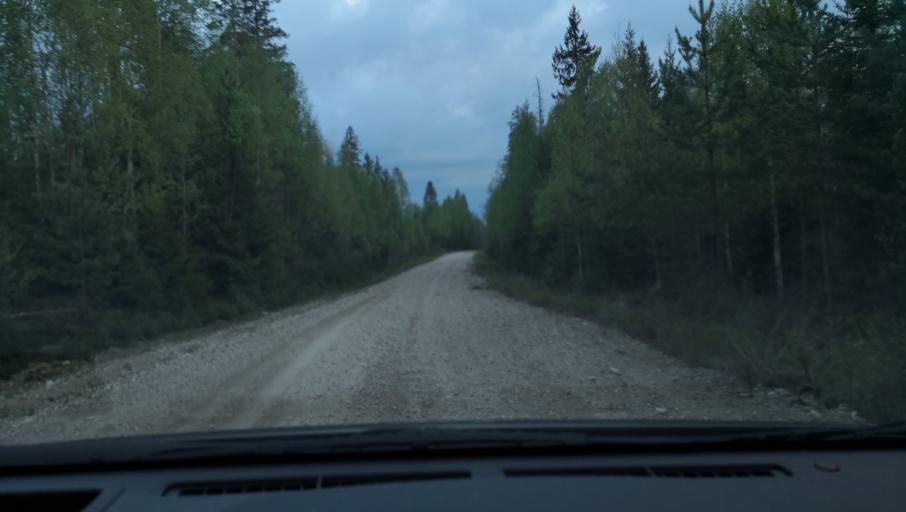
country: SE
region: Vaestmanland
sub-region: Skinnskattebergs Kommun
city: Skinnskatteberg
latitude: 59.7751
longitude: 15.4544
